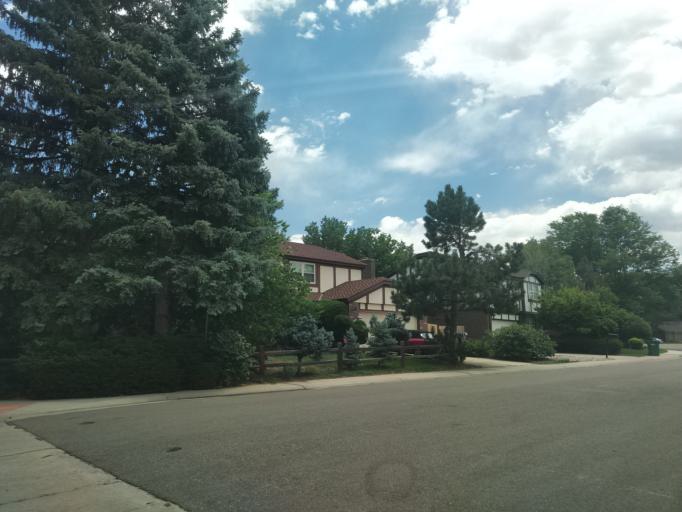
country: US
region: Colorado
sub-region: Jefferson County
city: Lakewood
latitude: 39.6796
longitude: -105.1031
